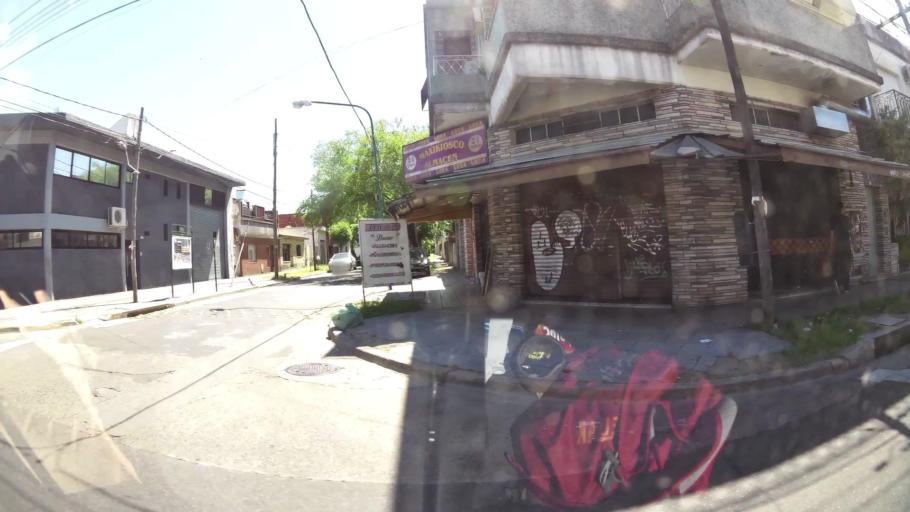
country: AR
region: Buenos Aires
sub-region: Partido de General San Martin
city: General San Martin
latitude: -34.5292
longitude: -58.5485
